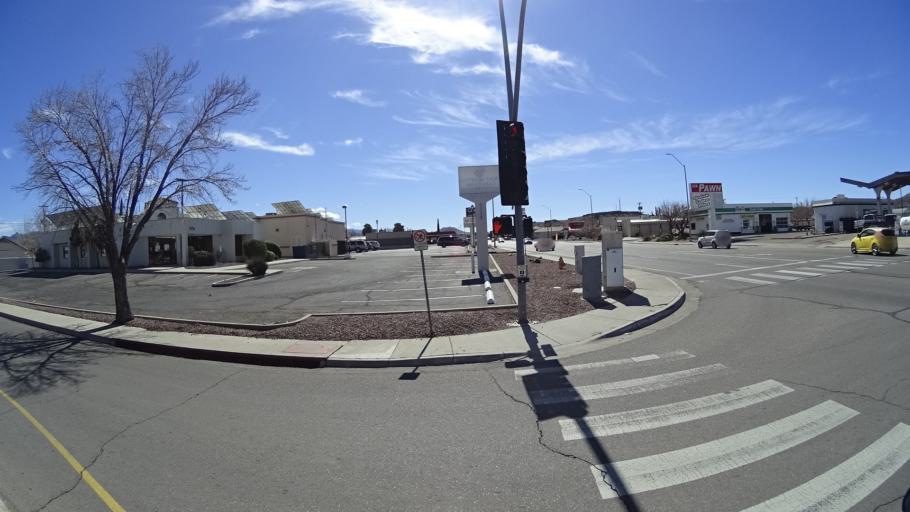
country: US
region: Arizona
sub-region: Mohave County
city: Kingman
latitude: 35.2140
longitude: -114.0349
